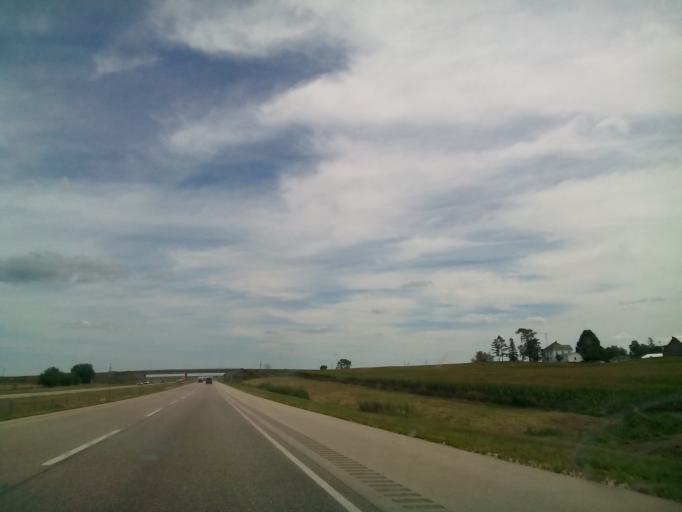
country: US
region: Illinois
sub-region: DeKalb County
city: Malta
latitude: 41.8993
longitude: -88.9300
